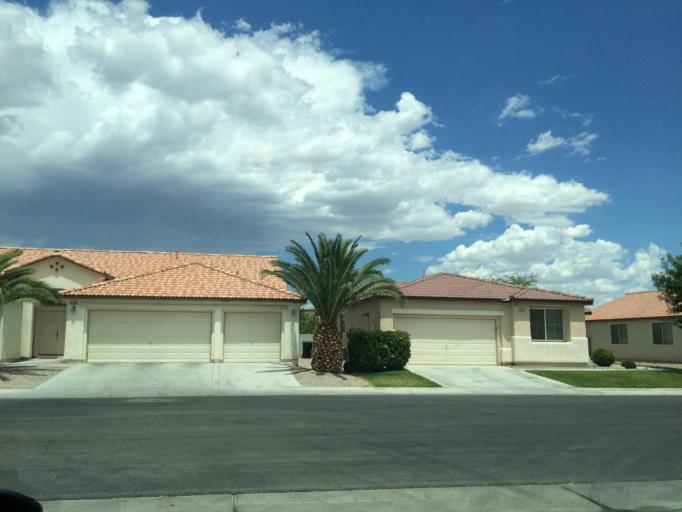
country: US
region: Nevada
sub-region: Clark County
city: North Las Vegas
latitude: 36.2586
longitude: -115.1833
